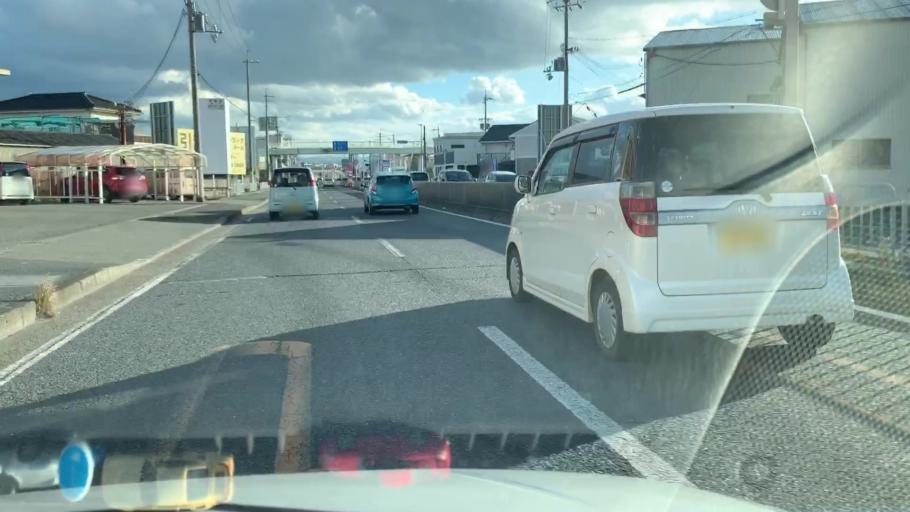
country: JP
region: Wakayama
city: Wakayama-shi
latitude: 34.2477
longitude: 135.1499
